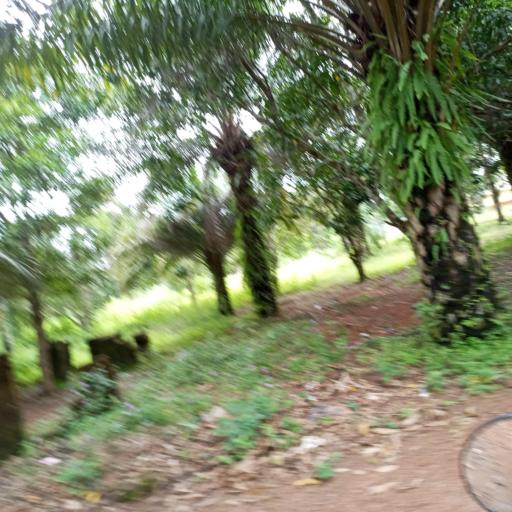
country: SL
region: Northern Province
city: Kambia
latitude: 9.1184
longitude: -12.9149
